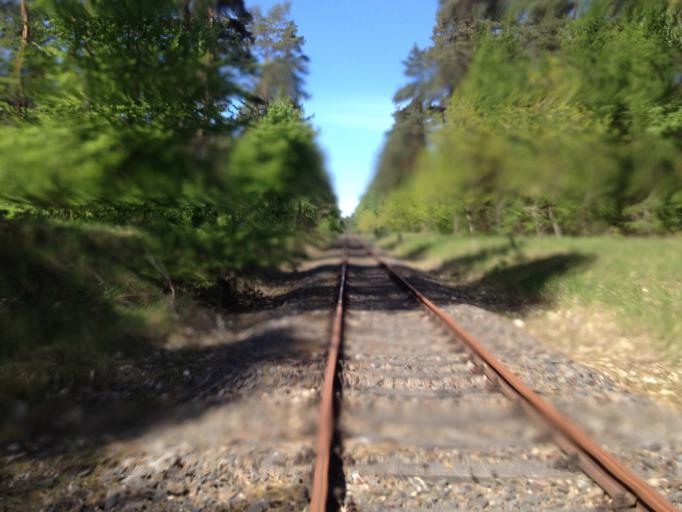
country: DE
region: Brandenburg
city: Lychen
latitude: 53.1637
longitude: 13.3765
